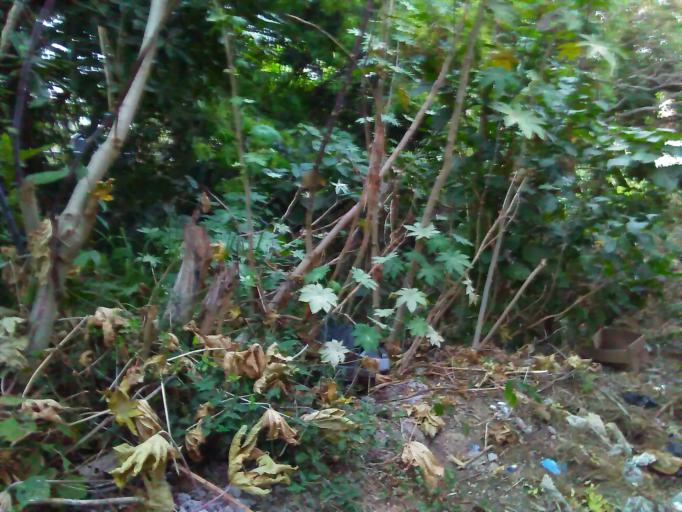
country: MX
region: Nayarit
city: Tepic
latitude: 21.5097
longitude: -104.9203
